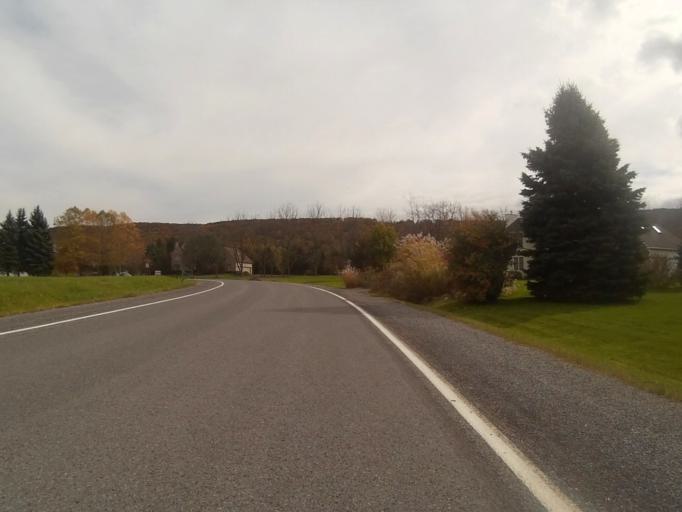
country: US
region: Pennsylvania
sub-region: Centre County
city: Boalsburg
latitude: 40.7752
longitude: -77.7597
